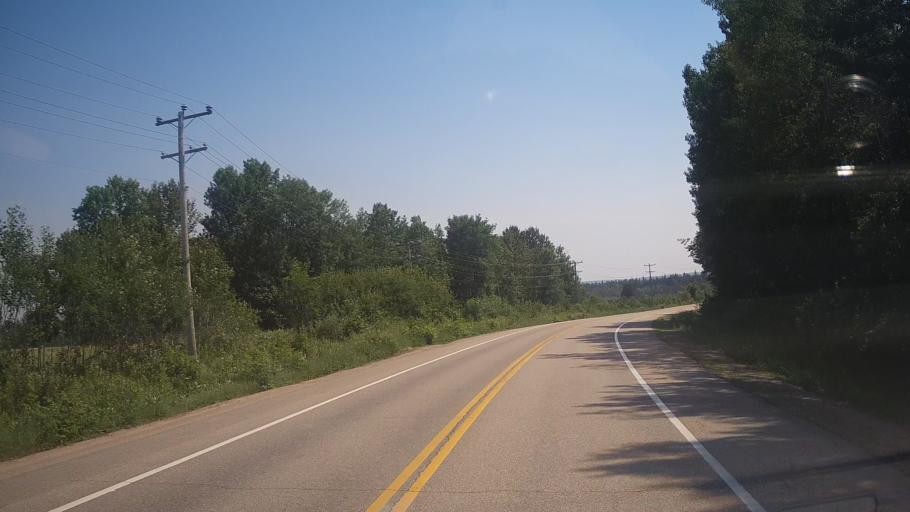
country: CA
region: Ontario
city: Pembroke
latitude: 45.8299
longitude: -77.0134
